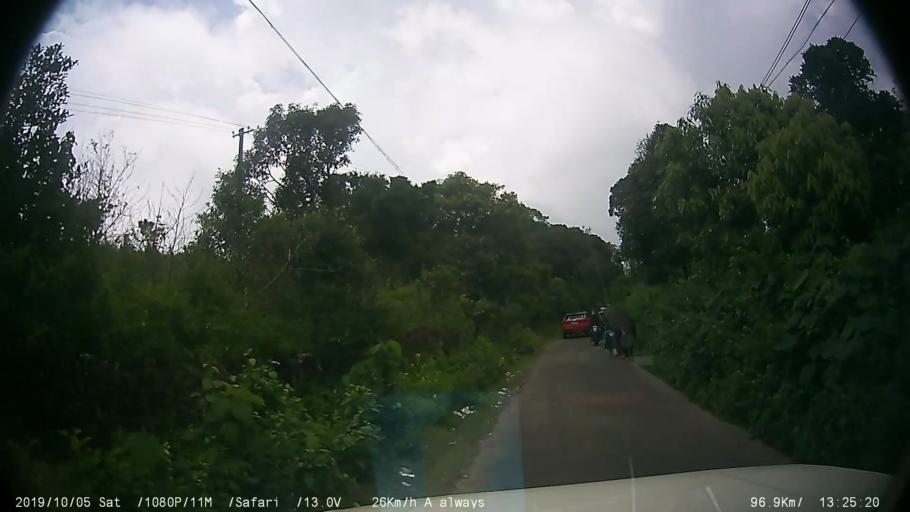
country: IN
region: Kerala
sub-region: Kottayam
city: Erattupetta
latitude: 9.5777
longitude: 76.9703
